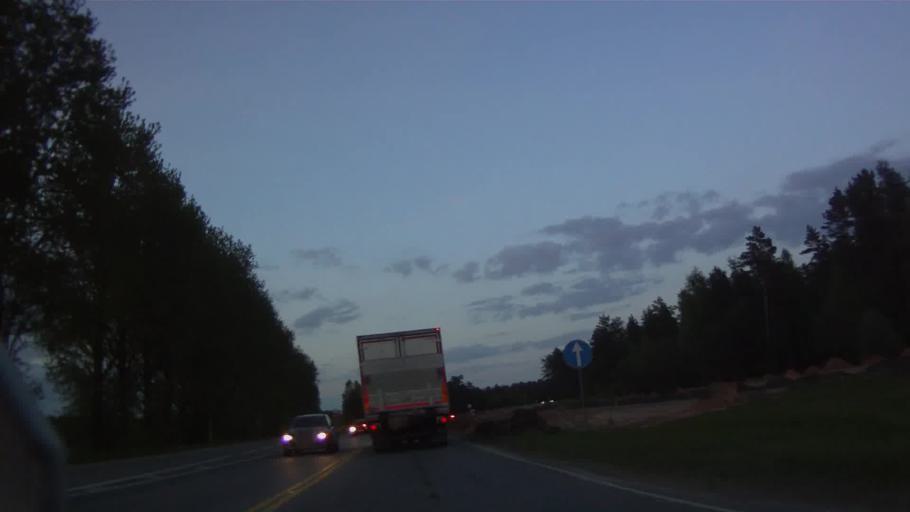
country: LV
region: Garkalne
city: Garkalne
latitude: 57.0382
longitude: 24.3953
